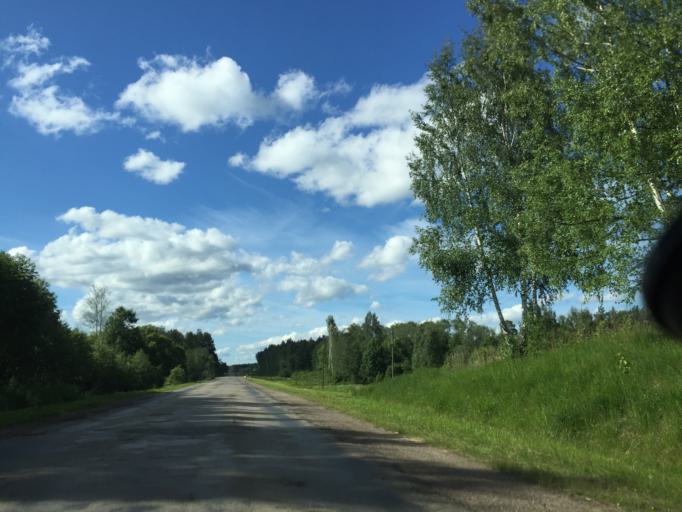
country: LV
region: Vecumnieki
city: Vecumnieki
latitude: 56.4184
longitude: 24.6276
